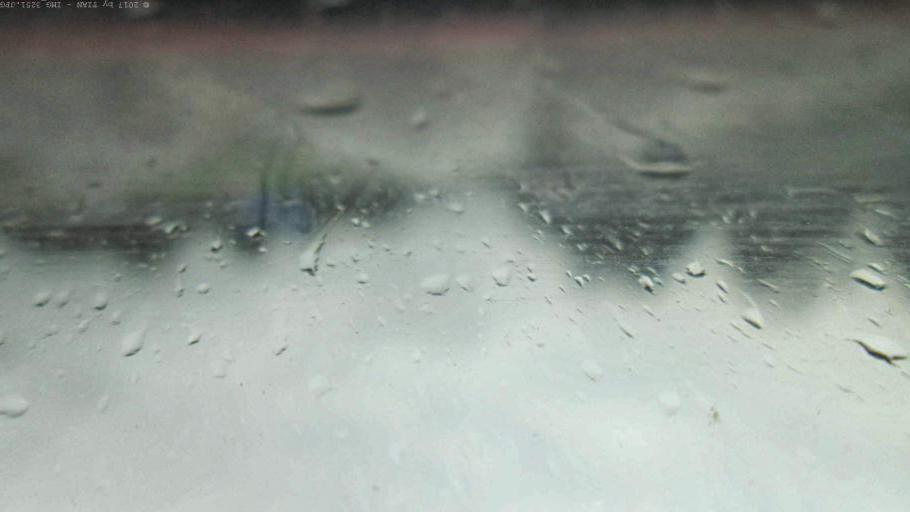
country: DE
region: Schleswig-Holstein
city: Ottenbuttel
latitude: 53.9588
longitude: 9.4911
